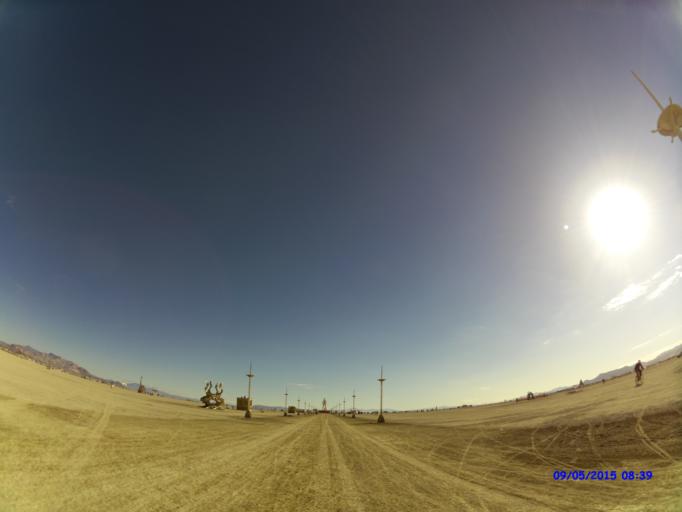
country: US
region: Nevada
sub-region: Pershing County
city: Lovelock
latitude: 40.7833
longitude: -119.2105
